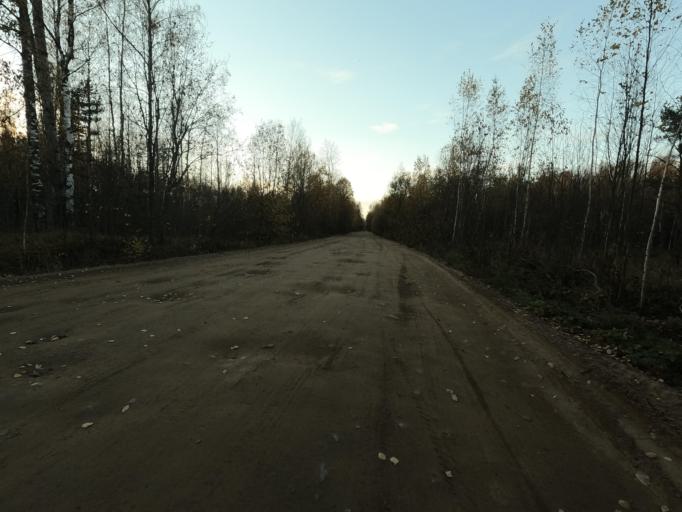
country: RU
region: Leningrad
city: Mga
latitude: 59.7564
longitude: 31.2755
